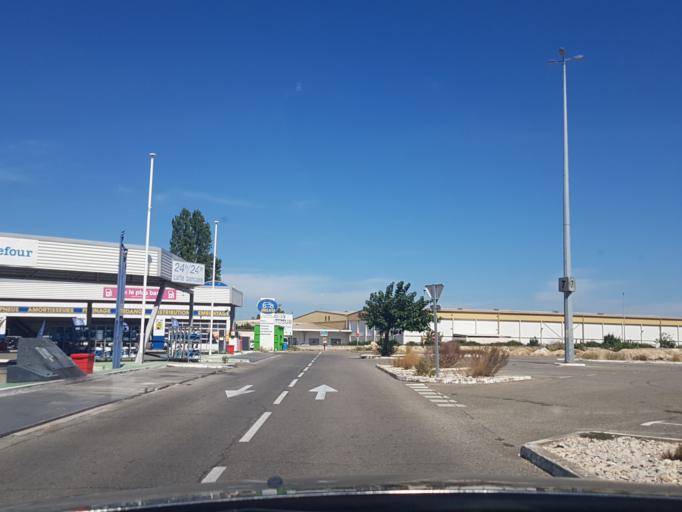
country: FR
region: Provence-Alpes-Cote d'Azur
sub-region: Departement du Vaucluse
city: Avignon
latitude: 43.9290
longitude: 4.7909
